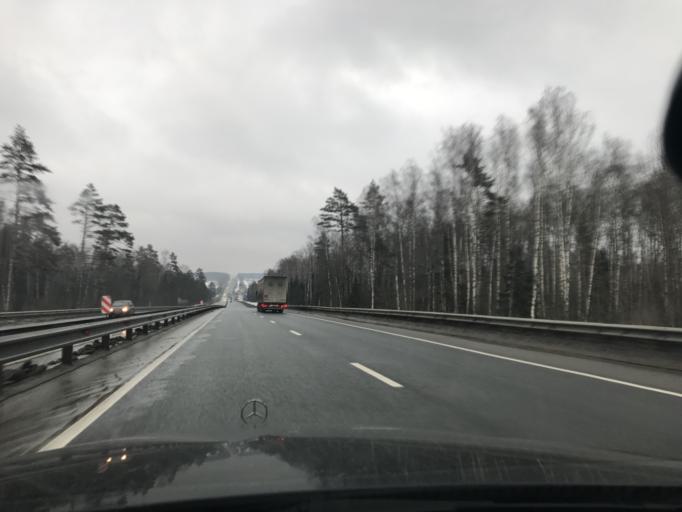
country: RU
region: Vladimir
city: Melekhovo
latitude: 56.2113
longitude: 41.3059
